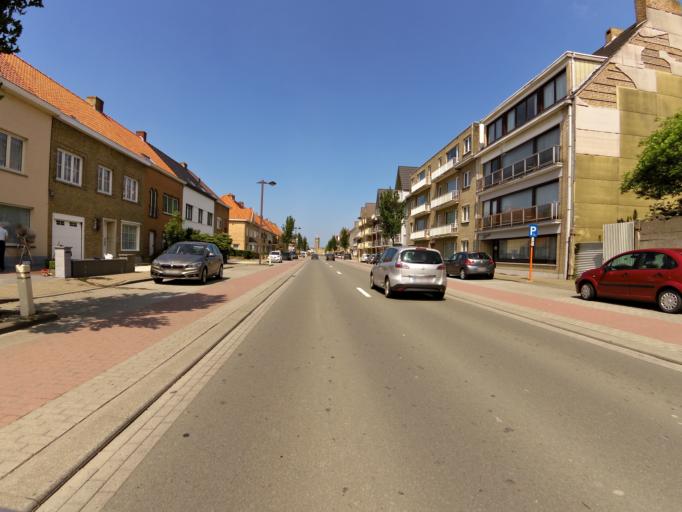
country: BE
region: Flanders
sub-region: Provincie West-Vlaanderen
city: Nieuwpoort
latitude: 51.1308
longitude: 2.7477
